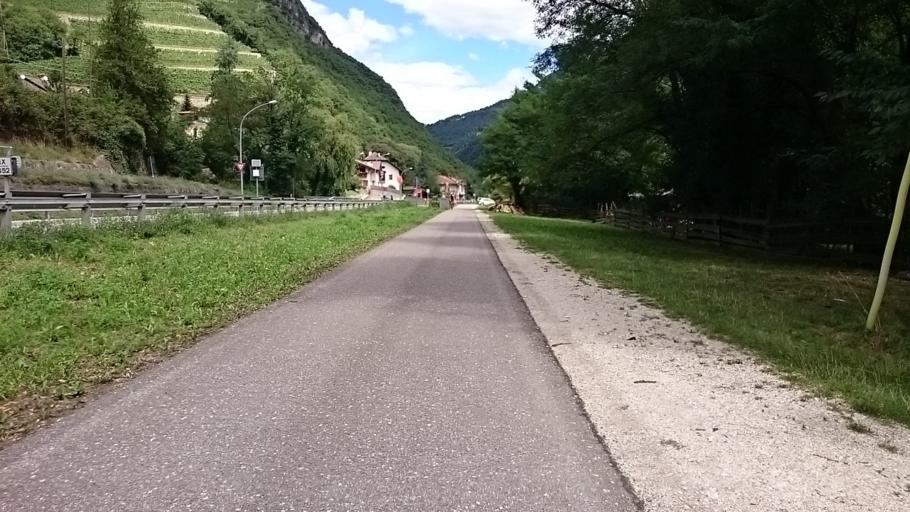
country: IT
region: Trentino-Alto Adige
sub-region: Bolzano
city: Fie Allo Sciliar
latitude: 46.5336
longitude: 11.4920
